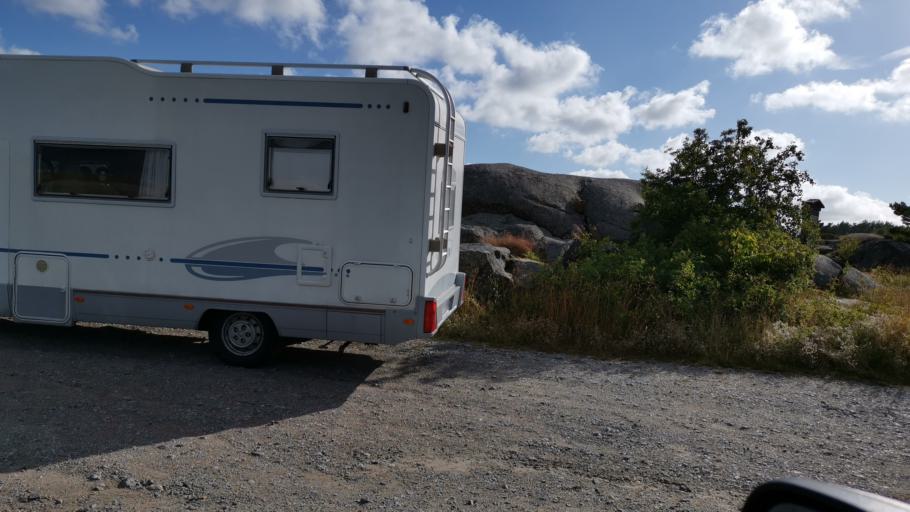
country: SE
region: Vaestra Goetaland
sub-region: Tjorns Kommun
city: Myggenas
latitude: 58.1093
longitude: 11.6544
